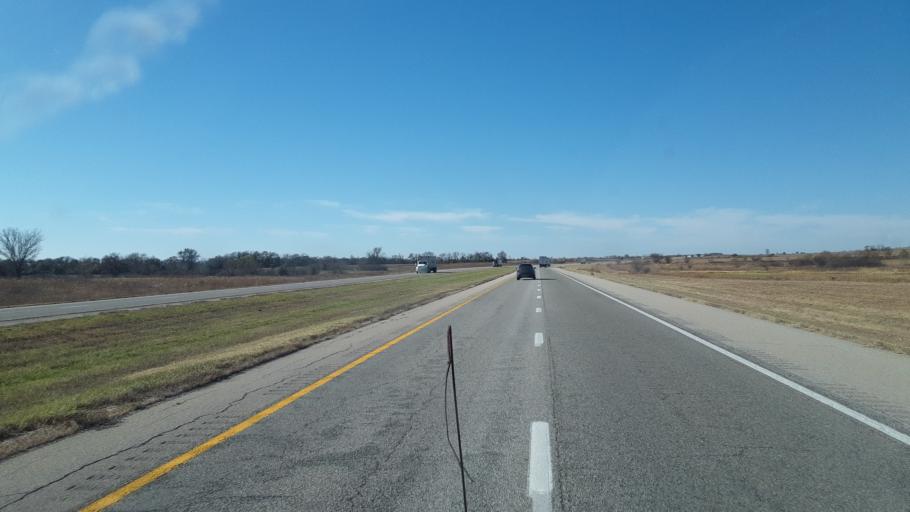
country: US
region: Kansas
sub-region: Osage County
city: Osage City
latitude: 38.4166
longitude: -95.9231
